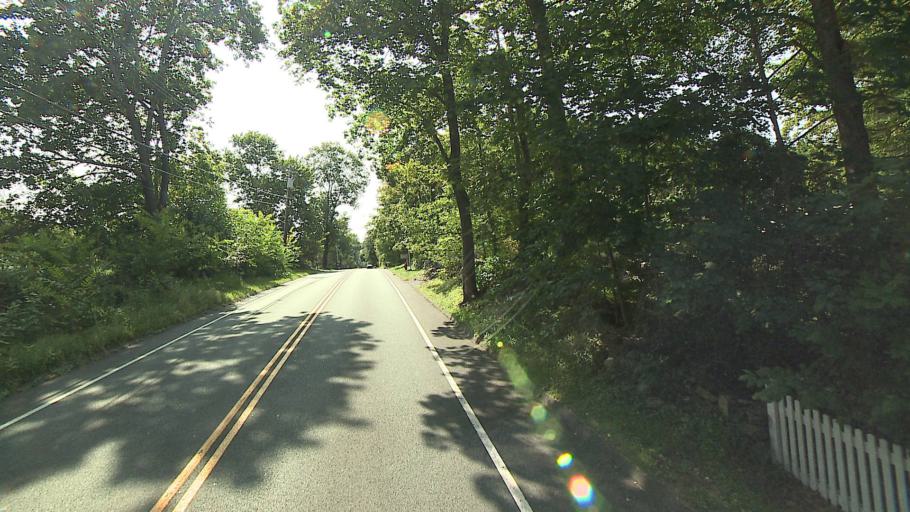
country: US
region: Connecticut
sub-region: Fairfield County
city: Newtown
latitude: 41.4561
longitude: -73.3817
